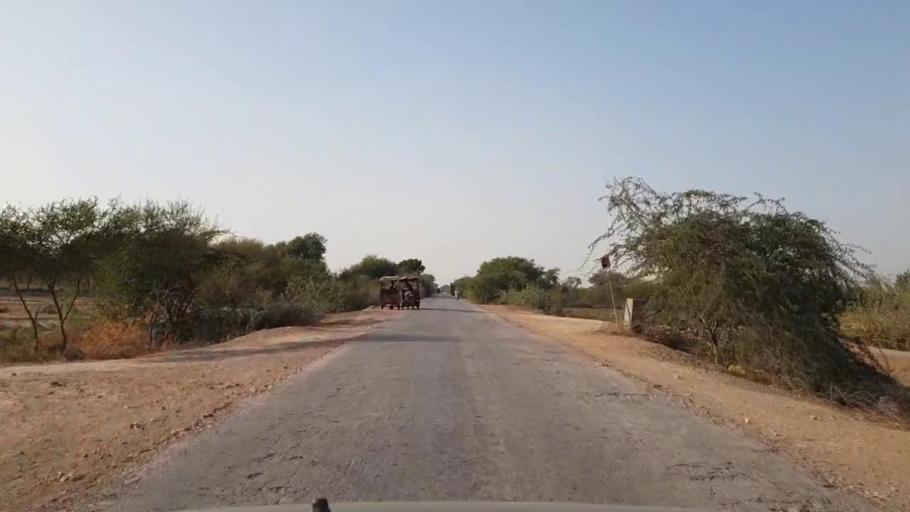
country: PK
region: Sindh
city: Tando Ghulam Ali
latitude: 25.1922
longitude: 68.8066
